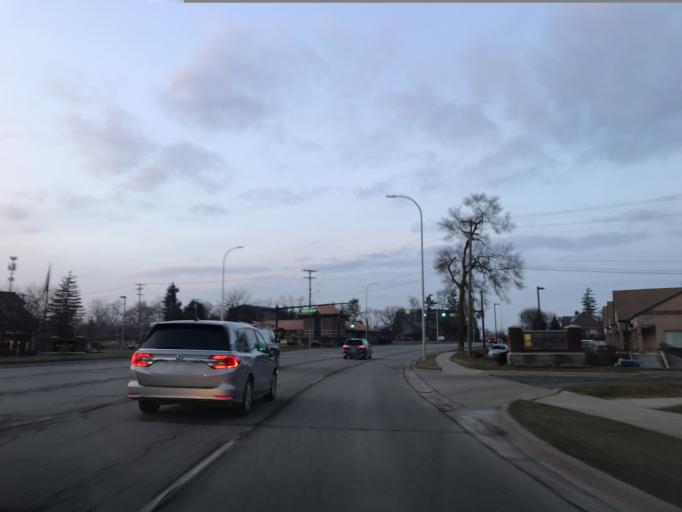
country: US
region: Michigan
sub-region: Livingston County
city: Brighton
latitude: 42.5253
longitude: -83.7775
